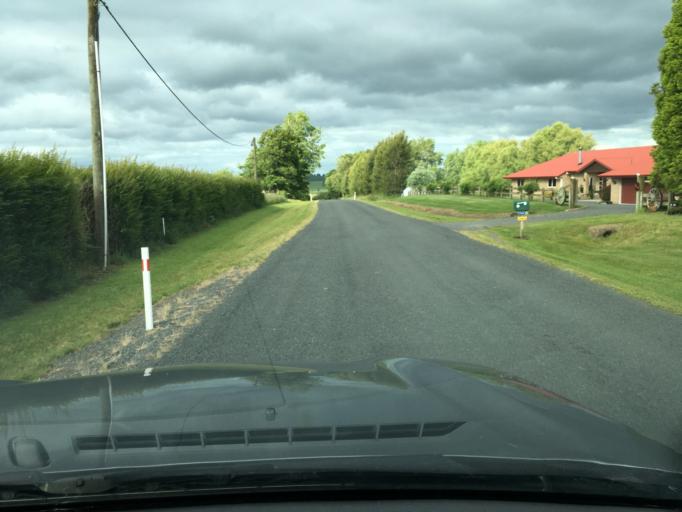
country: NZ
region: Waikato
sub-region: Hamilton City
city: Hamilton
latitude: -37.8228
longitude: 175.1748
